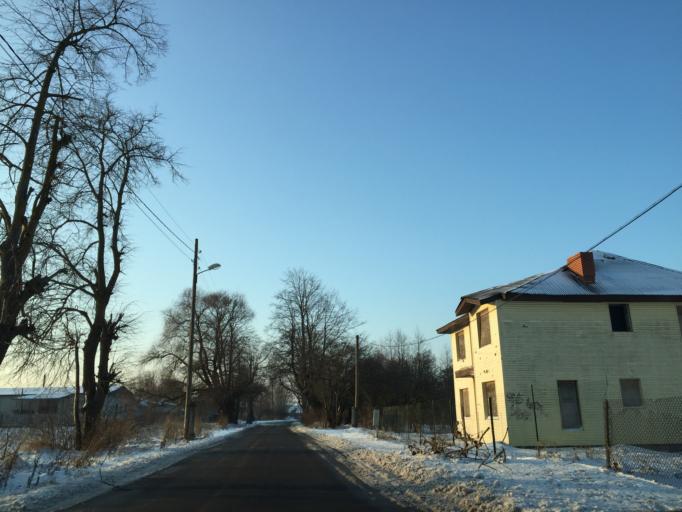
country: LV
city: Tireli
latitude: 56.9379
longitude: 23.6102
